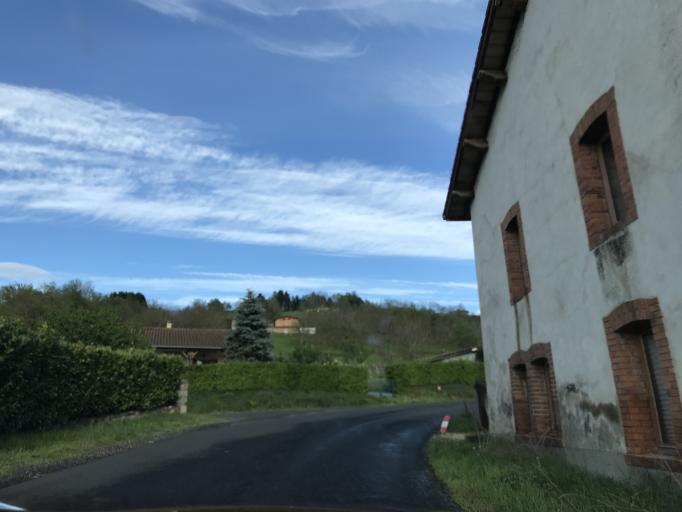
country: FR
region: Auvergne
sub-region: Departement du Puy-de-Dome
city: Escoutoux
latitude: 45.7785
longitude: 3.5942
